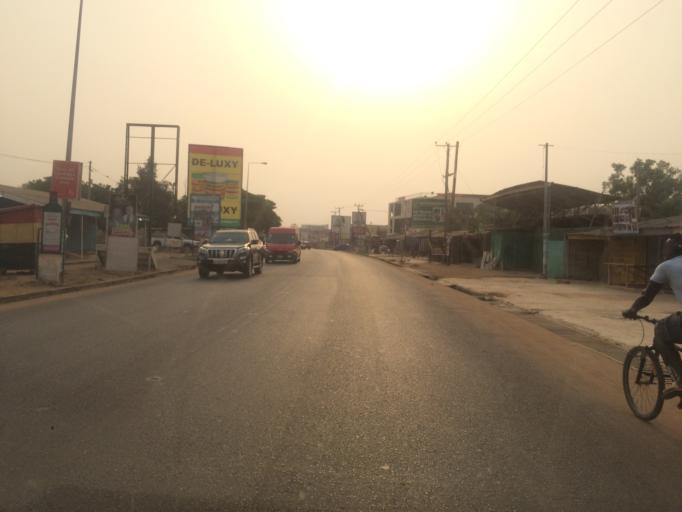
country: GH
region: Greater Accra
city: Nungua
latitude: 5.6265
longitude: -0.0839
